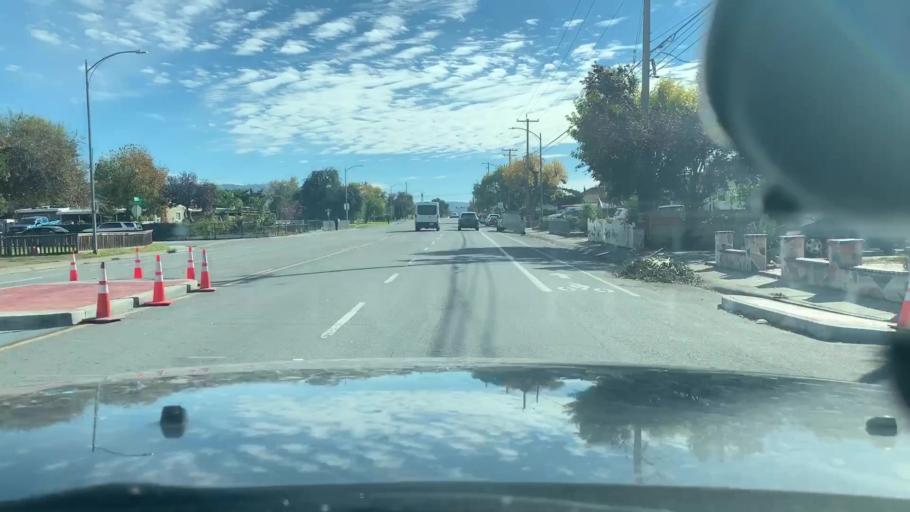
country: US
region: California
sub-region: Santa Clara County
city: Alum Rock
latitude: 37.3542
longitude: -121.8175
